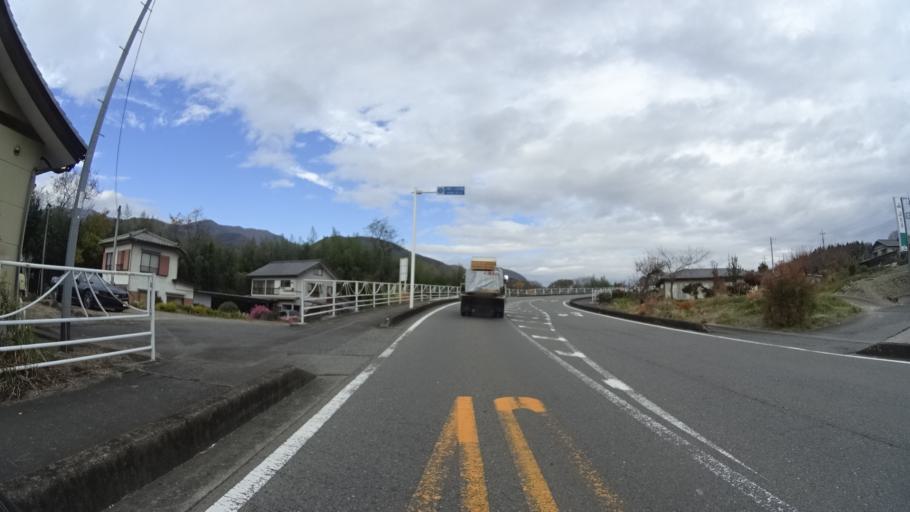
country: JP
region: Gunma
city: Shibukawa
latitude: 36.5462
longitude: 139.0323
